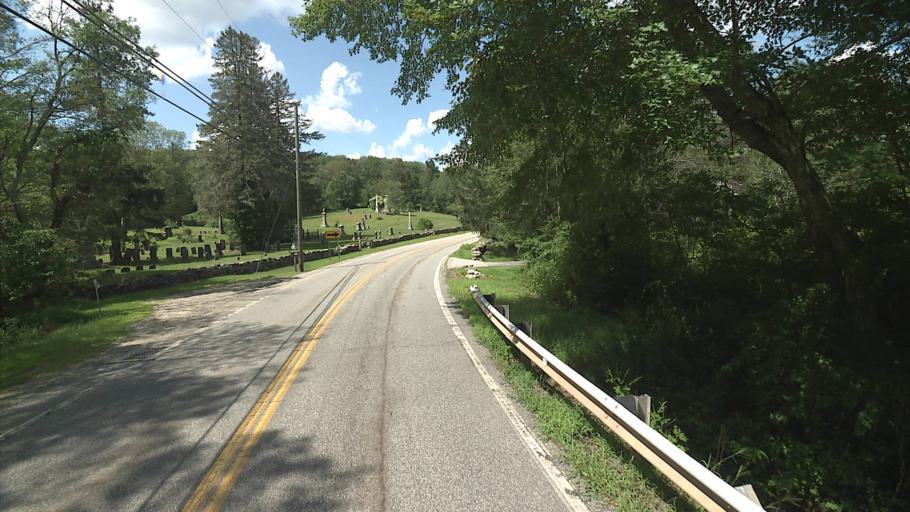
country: US
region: Connecticut
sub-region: Tolland County
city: Storrs
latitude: 41.8180
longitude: -72.1719
